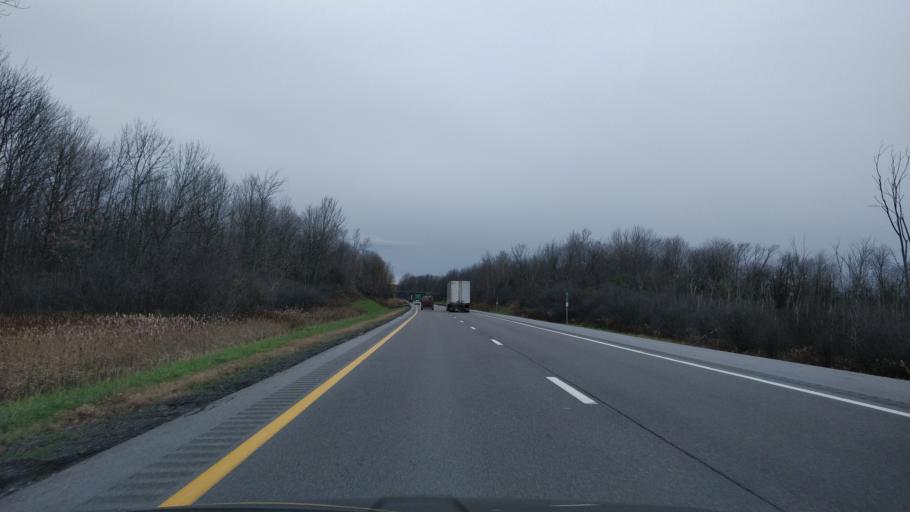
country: US
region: New York
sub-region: Oswego County
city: Pulaski
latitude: 43.5909
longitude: -76.1060
